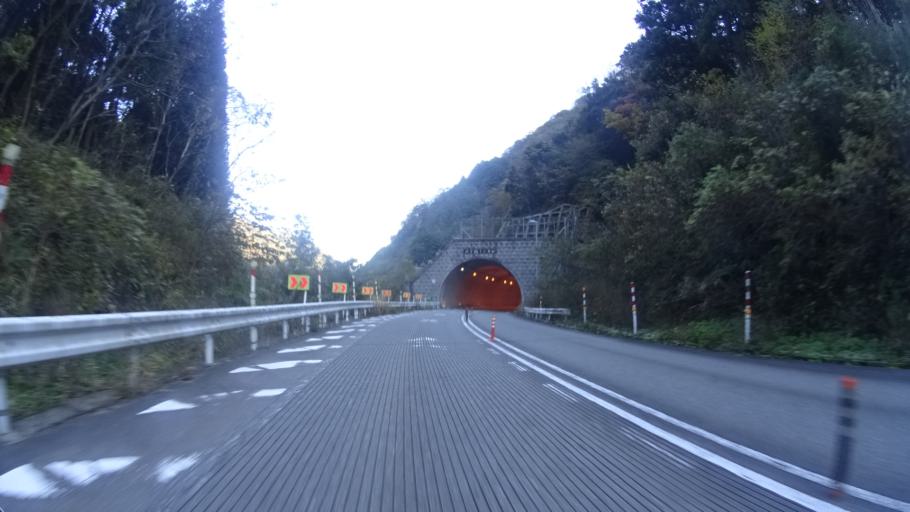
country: JP
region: Fukui
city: Maruoka
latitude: 36.1948
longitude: 136.3448
